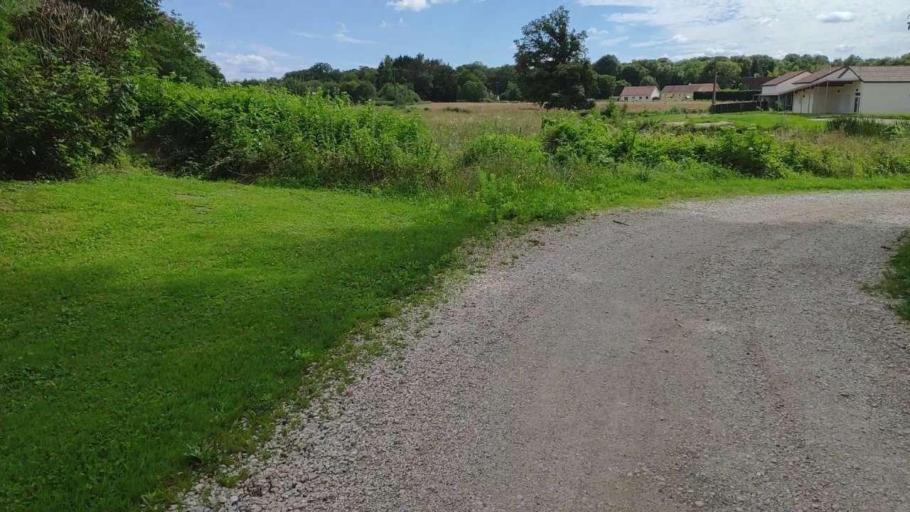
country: FR
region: Franche-Comte
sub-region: Departement du Jura
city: Bletterans
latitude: 46.8007
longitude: 5.4492
